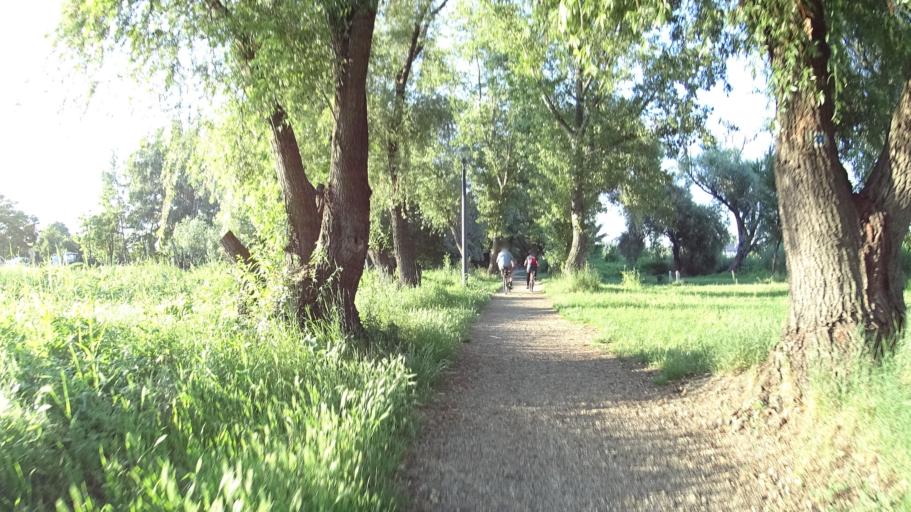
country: HU
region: Budapest
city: Budapest XXIII. keruelet
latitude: 47.3912
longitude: 19.1073
